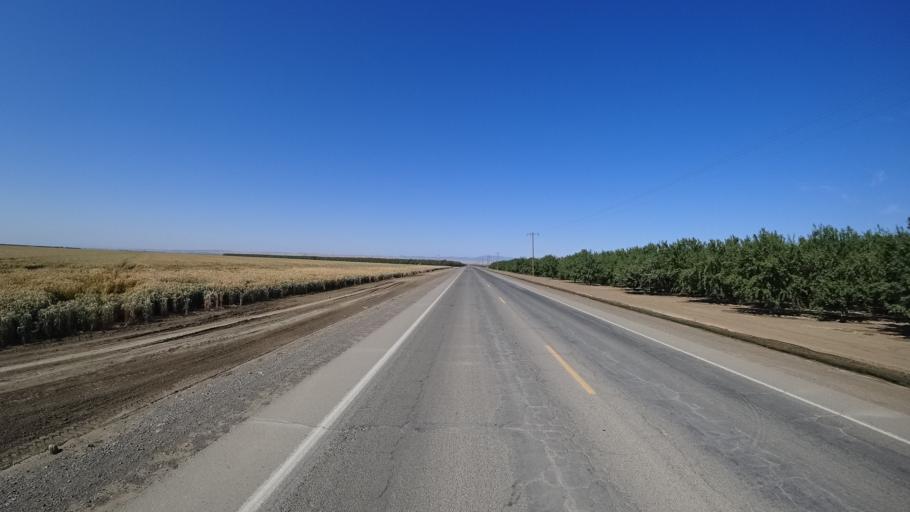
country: US
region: California
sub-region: Kings County
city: Lemoore Station
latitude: 36.1667
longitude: -119.9744
